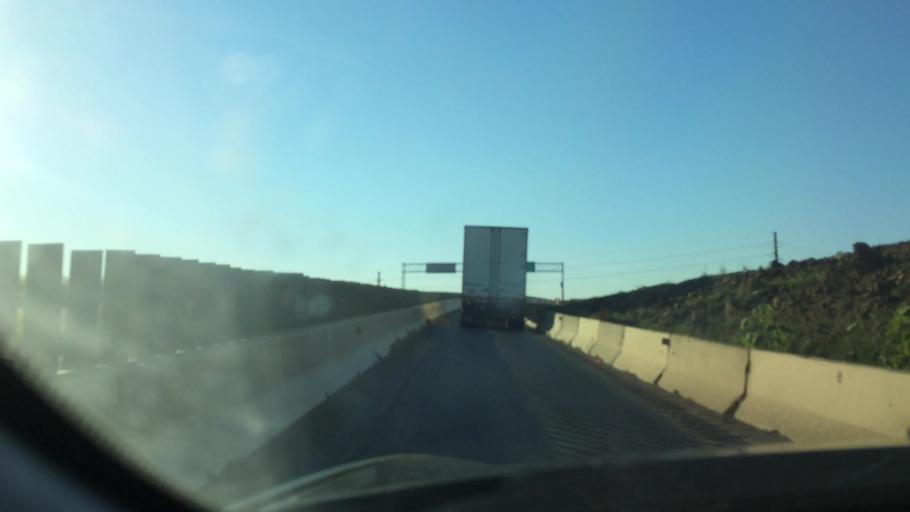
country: US
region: Ohio
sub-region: Hancock County
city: Findlay
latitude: 41.0256
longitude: -83.6720
